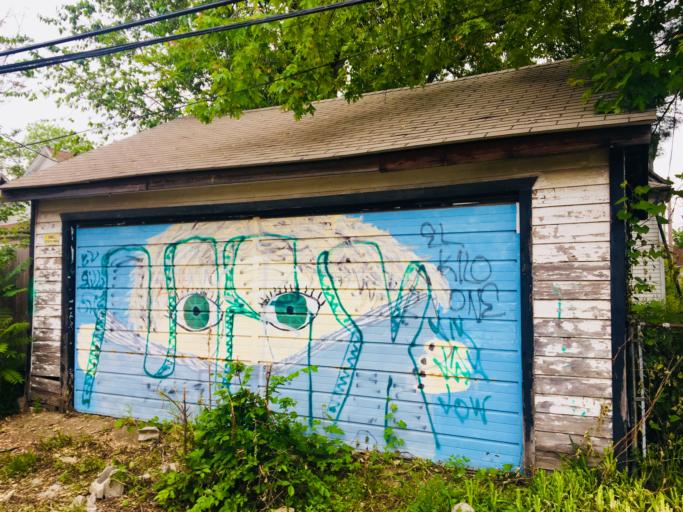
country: US
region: Michigan
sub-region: Wayne County
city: River Rouge
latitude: 42.3130
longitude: -83.1317
